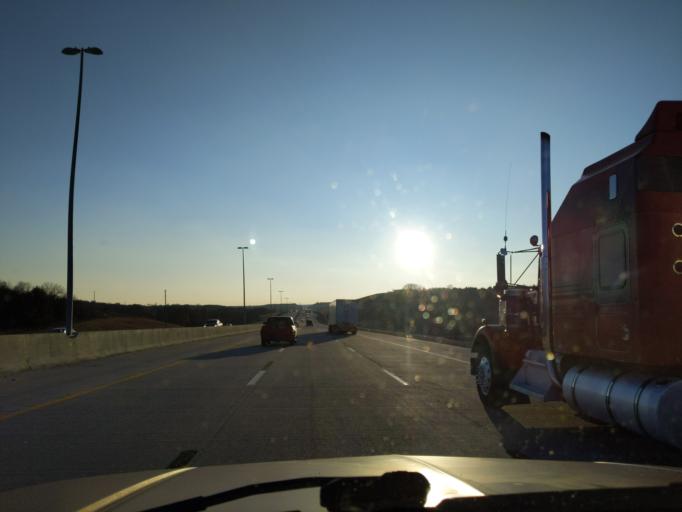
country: US
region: Oklahoma
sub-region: Creek County
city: Kellyville
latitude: 35.9795
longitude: -96.2053
